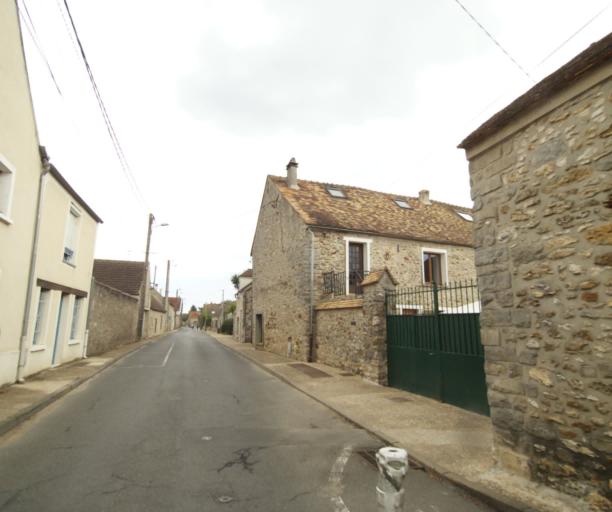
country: FR
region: Ile-de-France
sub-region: Departement de Seine-et-Marne
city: Perthes
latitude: 48.4778
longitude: 2.5521
